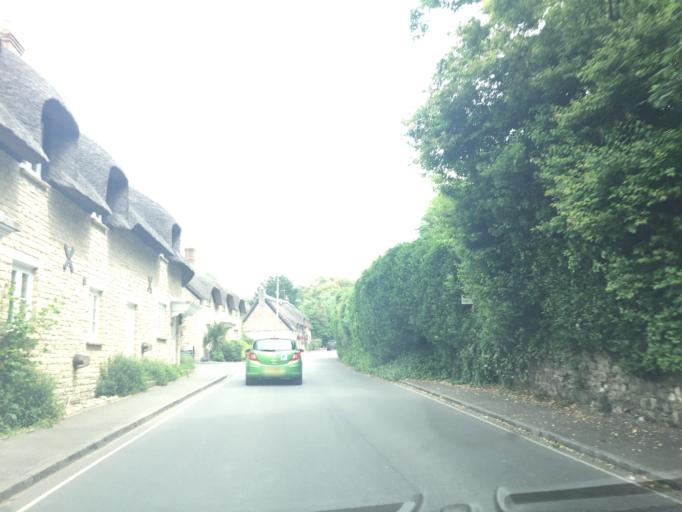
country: GB
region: England
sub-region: Dorset
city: Wool
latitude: 50.6252
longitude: -2.2500
